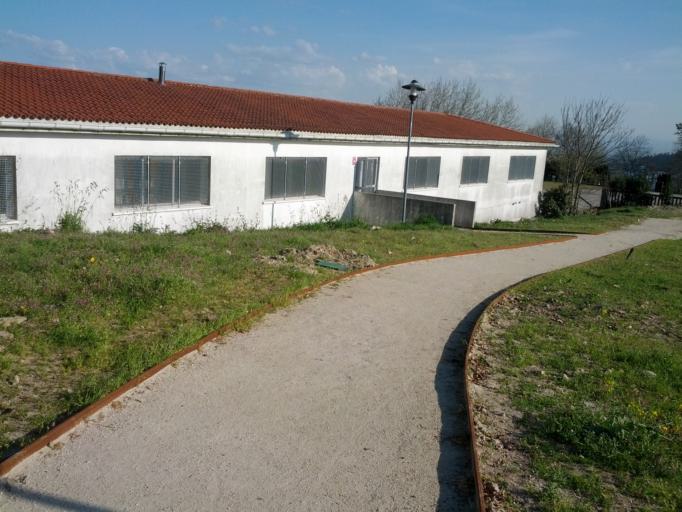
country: ES
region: Galicia
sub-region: Provincia da Coruna
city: Santiago de Compostela
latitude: 42.8856
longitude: -8.5369
